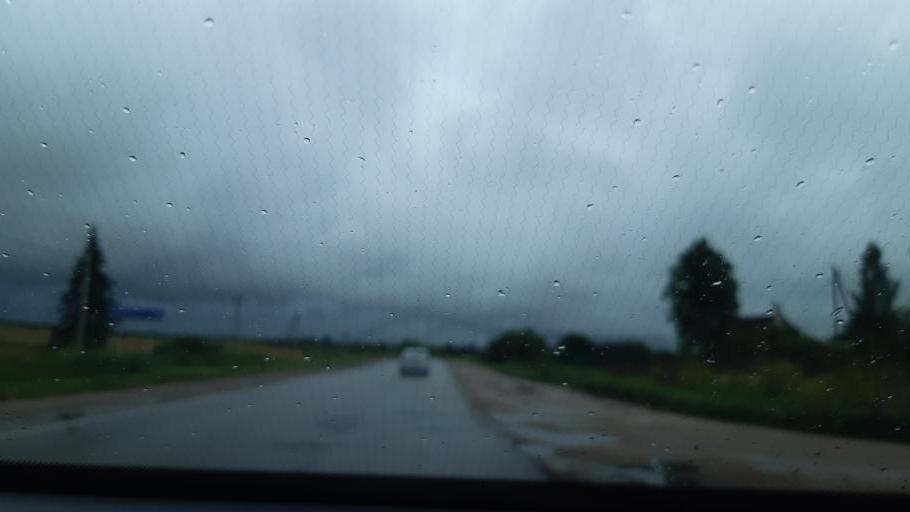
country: RU
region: Smolensk
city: Gagarin
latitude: 55.6196
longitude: 34.9663
